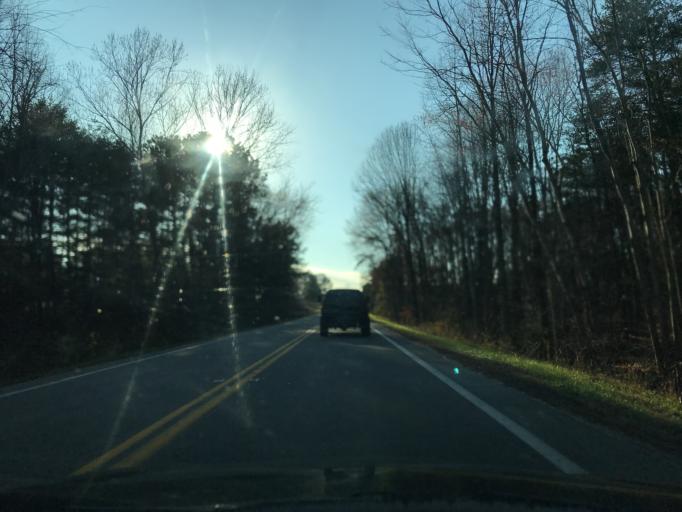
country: US
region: Virginia
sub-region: Prince Edward County
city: Farmville
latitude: 37.2732
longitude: -78.2778
